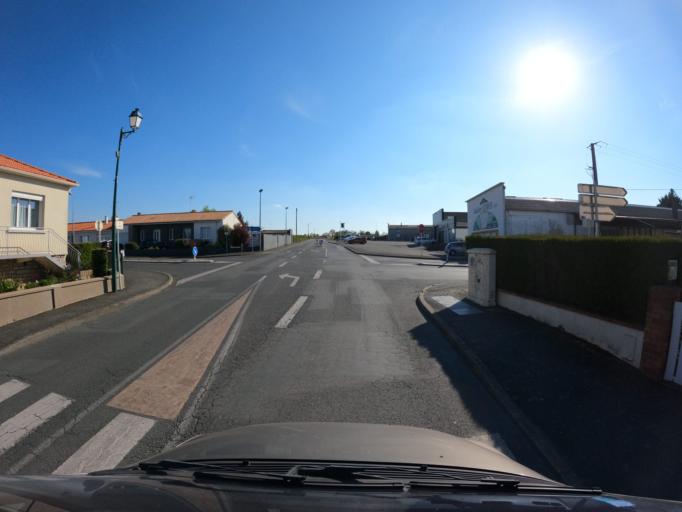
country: FR
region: Pays de la Loire
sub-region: Departement de la Vendee
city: La Verrie
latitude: 46.9574
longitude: -1.0014
